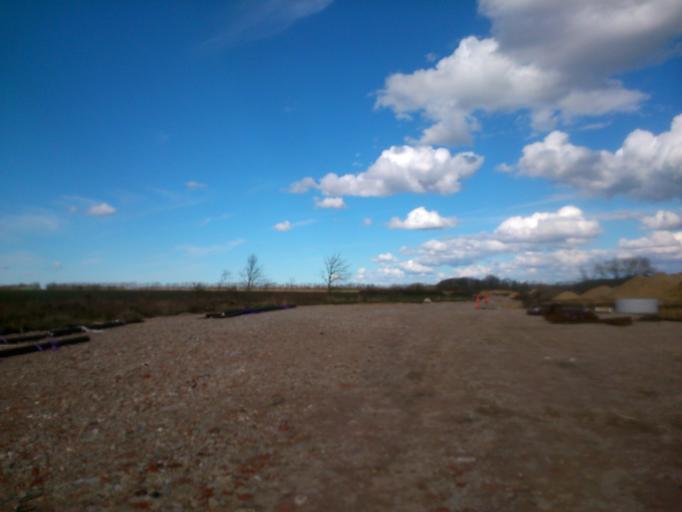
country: DK
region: Central Jutland
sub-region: Ringkobing-Skjern Kommune
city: Videbaek
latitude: 56.0201
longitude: 8.5800
